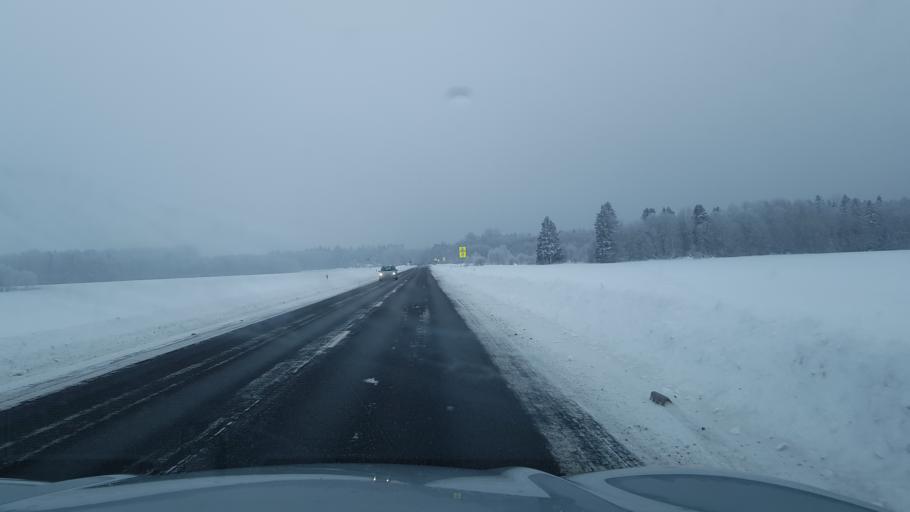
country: EE
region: Ida-Virumaa
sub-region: Johvi vald
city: Johvi
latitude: 59.3134
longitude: 27.3924
